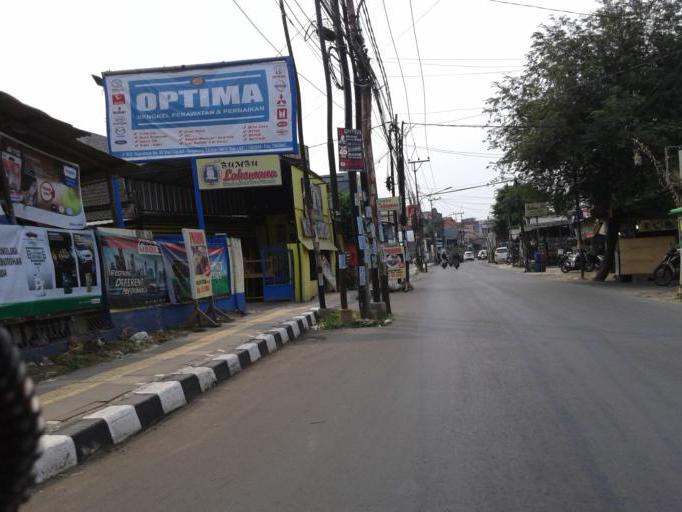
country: ID
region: Banten
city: South Tangerang
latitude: -6.2999
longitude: 106.7500
